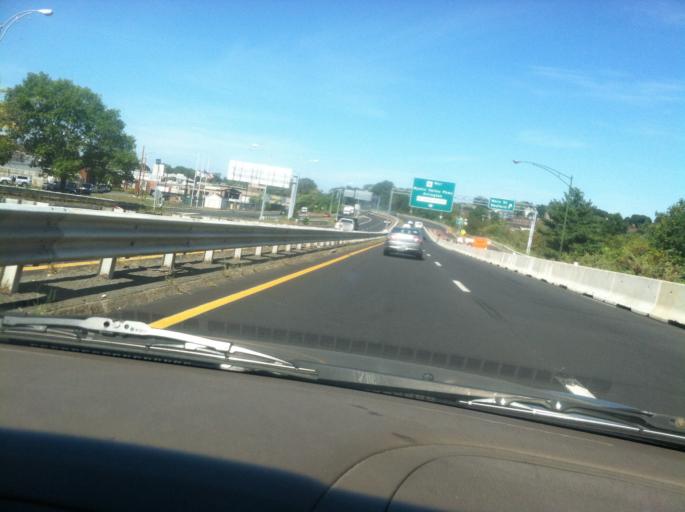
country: US
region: Massachusetts
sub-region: Suffolk County
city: Chelsea
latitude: 42.3884
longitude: -71.0401
